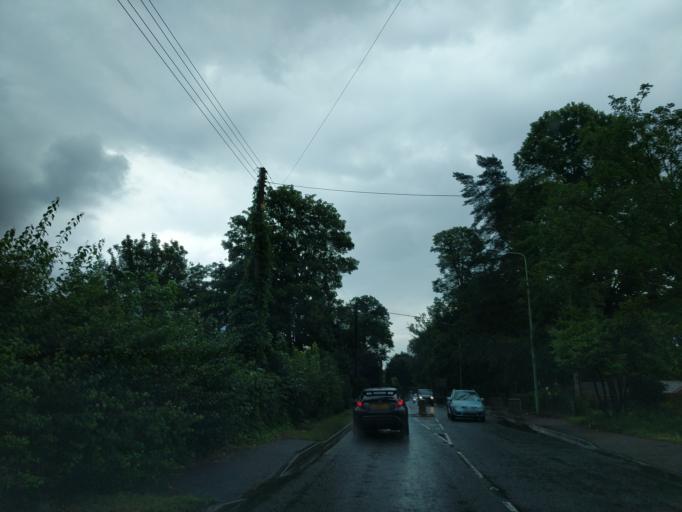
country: GB
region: England
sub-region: Suffolk
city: Lakenheath
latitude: 52.3442
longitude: 0.5237
